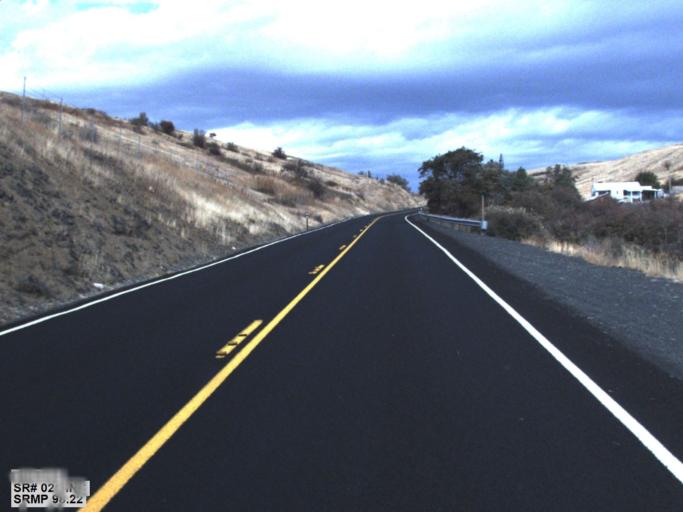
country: US
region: Washington
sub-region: Okanogan County
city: Coulee Dam
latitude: 47.8459
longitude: -118.7168
